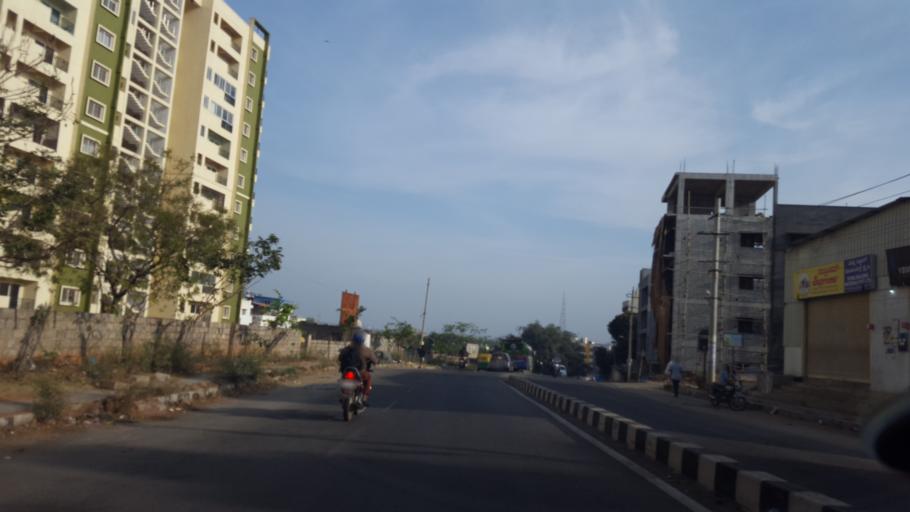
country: IN
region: Karnataka
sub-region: Bangalore Urban
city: Bangalore
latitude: 12.9174
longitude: 77.5133
